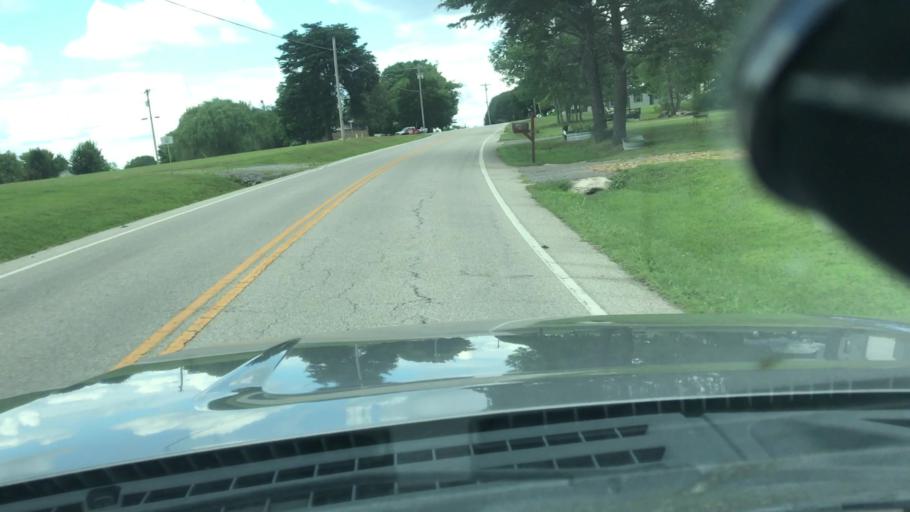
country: US
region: Tennessee
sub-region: Sumner County
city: Westmoreland
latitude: 36.5938
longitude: -86.3590
